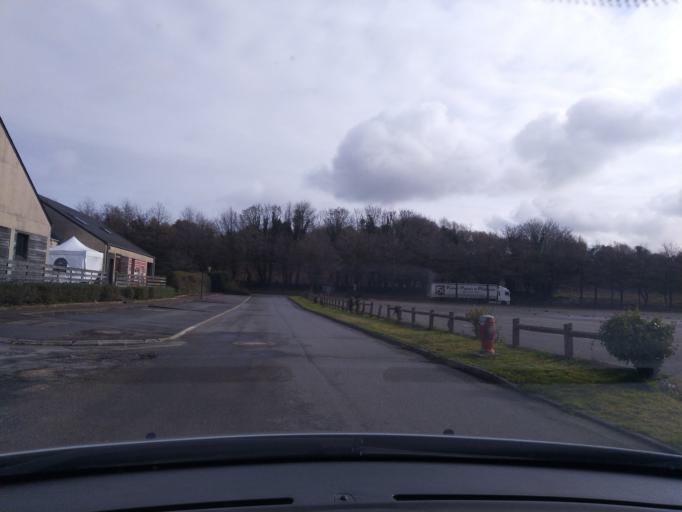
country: FR
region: Brittany
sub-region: Departement du Finistere
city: Guerlesquin
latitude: 48.5152
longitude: -3.5851
